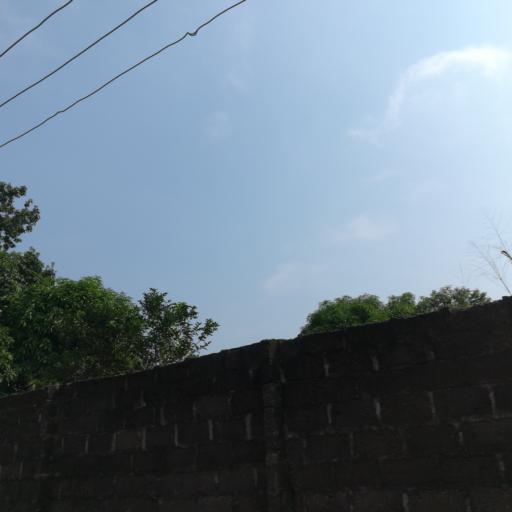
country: NG
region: Rivers
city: Port Harcourt
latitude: 4.8406
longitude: 7.0623
